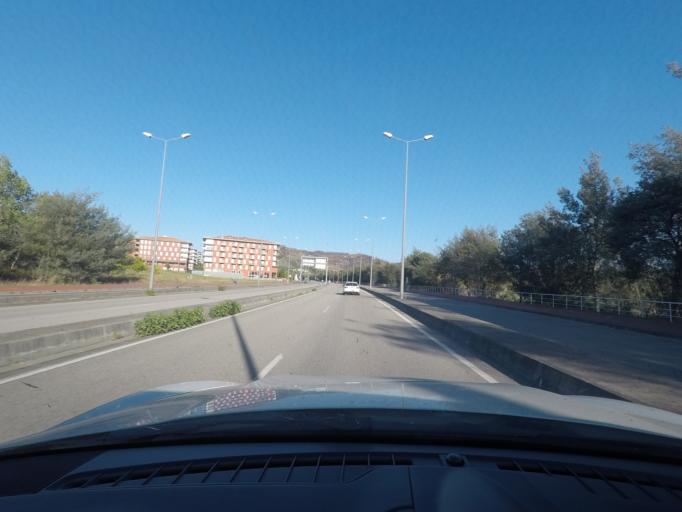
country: PT
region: Coimbra
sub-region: Coimbra
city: Coimbra
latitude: 40.1825
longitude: -8.4104
